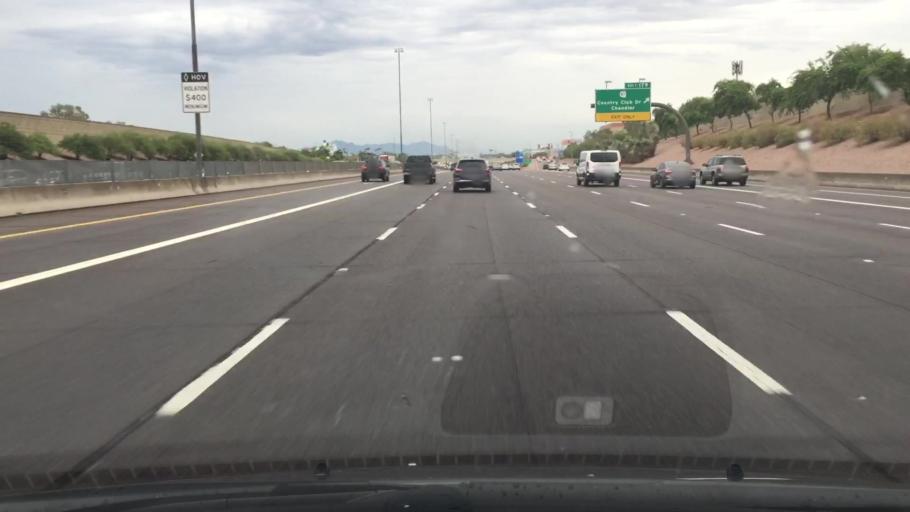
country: US
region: Arizona
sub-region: Maricopa County
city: Mesa
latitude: 33.3881
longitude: -111.8314
